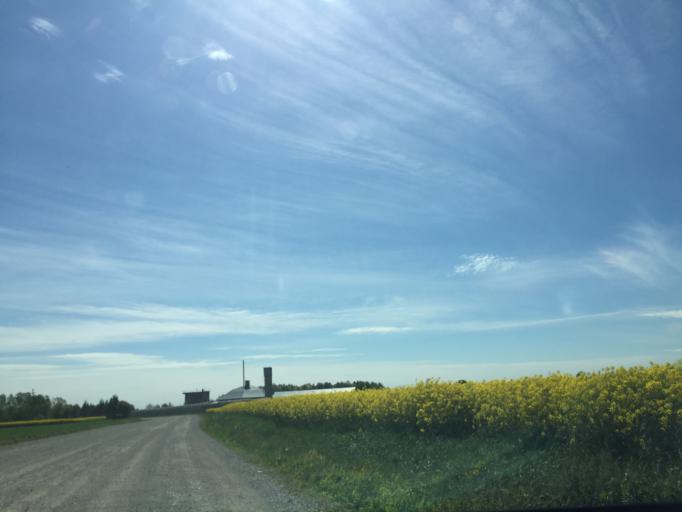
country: LT
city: Linkuva
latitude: 56.0718
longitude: 24.0703
